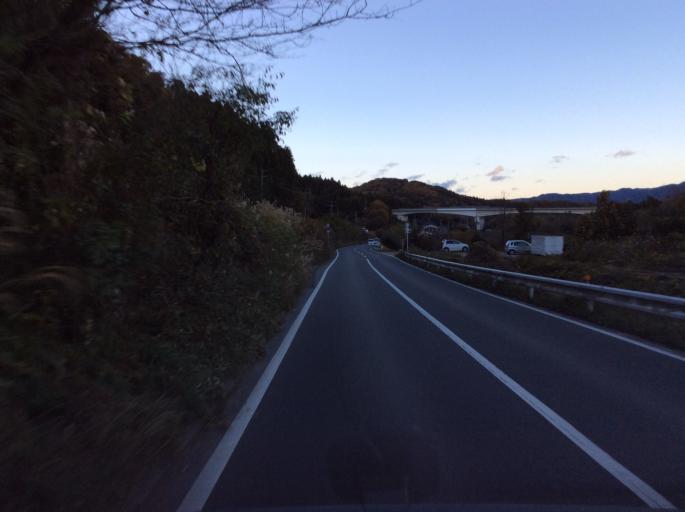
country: JP
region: Fukushima
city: Iwaki
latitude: 37.0913
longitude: 140.8619
